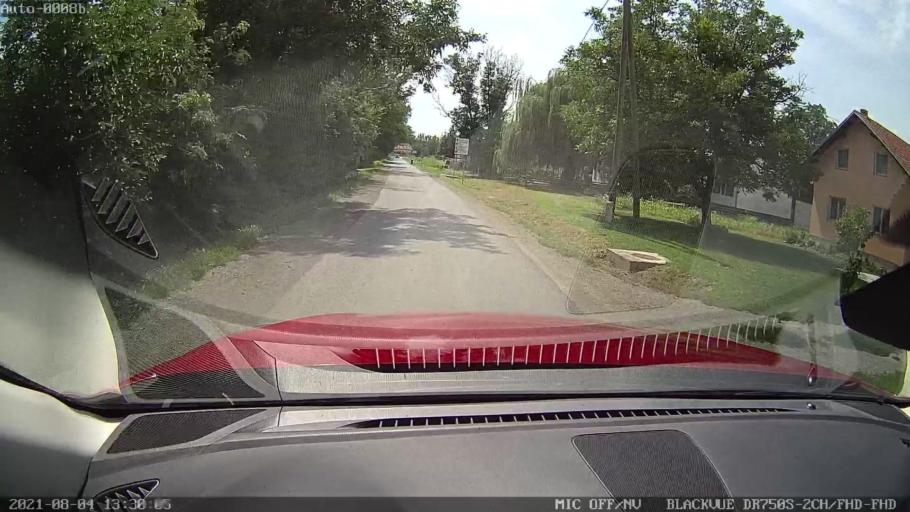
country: HR
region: Osjecko-Baranjska
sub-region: Grad Osijek
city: Bilje
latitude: 45.6014
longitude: 18.7819
